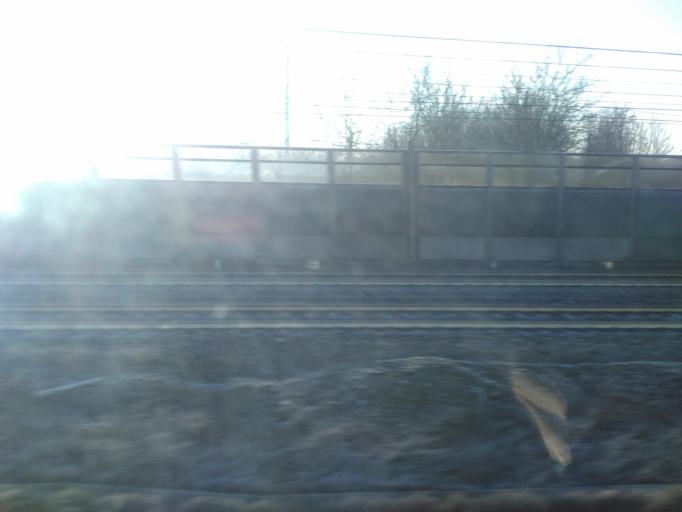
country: IT
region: Veneto
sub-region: Provincia di Venezia
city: Pianiga
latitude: 45.4406
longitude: 12.0070
